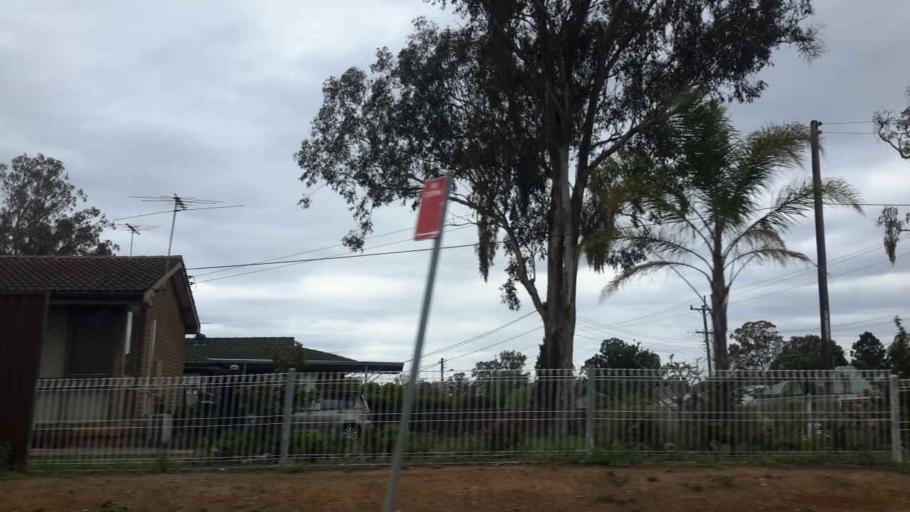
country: AU
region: New South Wales
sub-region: Penrith Municipality
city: Cambridge Park
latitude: -33.7433
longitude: 150.7155
